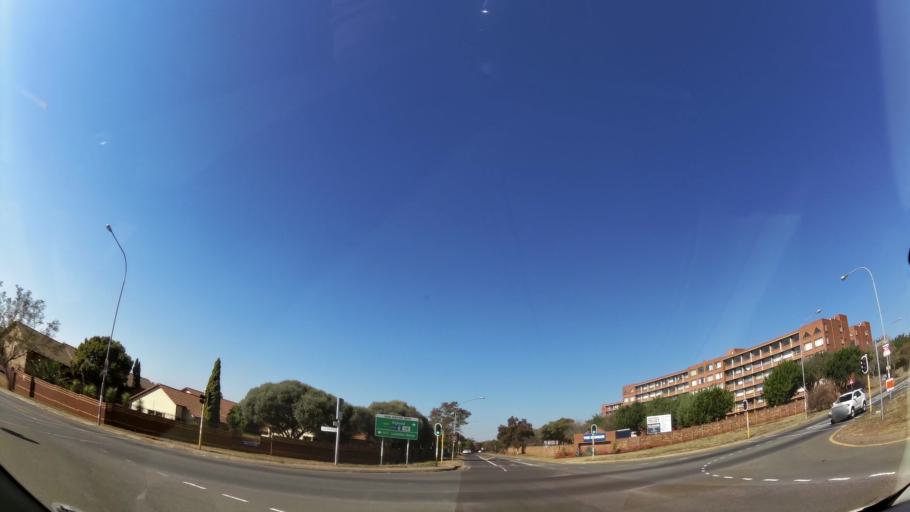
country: ZA
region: Gauteng
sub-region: City of Tshwane Metropolitan Municipality
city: Centurion
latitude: -25.8529
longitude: 28.1786
